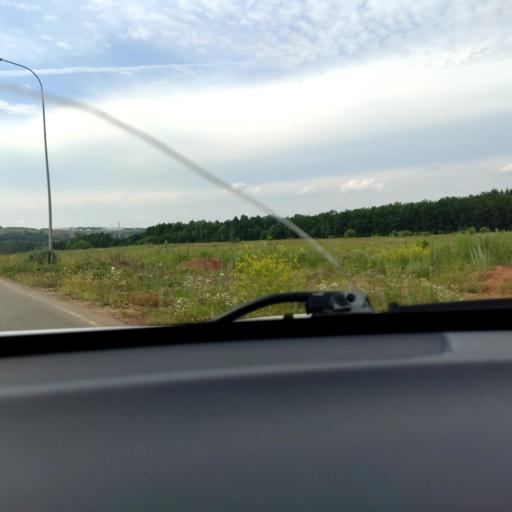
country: RU
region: Tatarstan
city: Sviyazhsk
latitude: 55.7424
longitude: 48.7755
